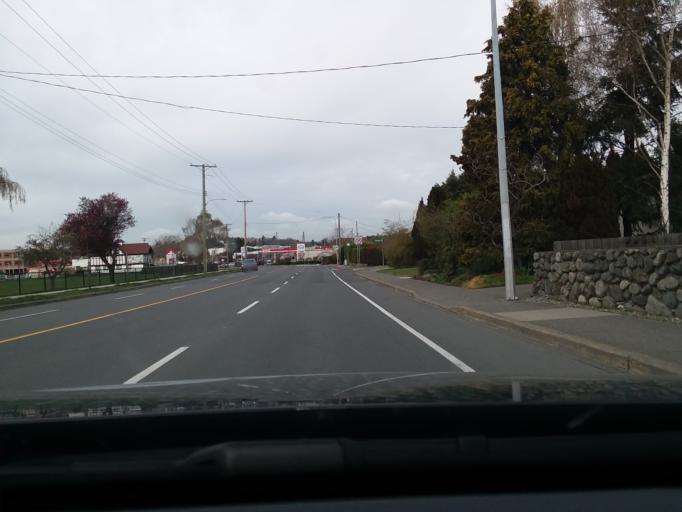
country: CA
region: British Columbia
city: Oak Bay
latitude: 48.4462
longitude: -123.3300
